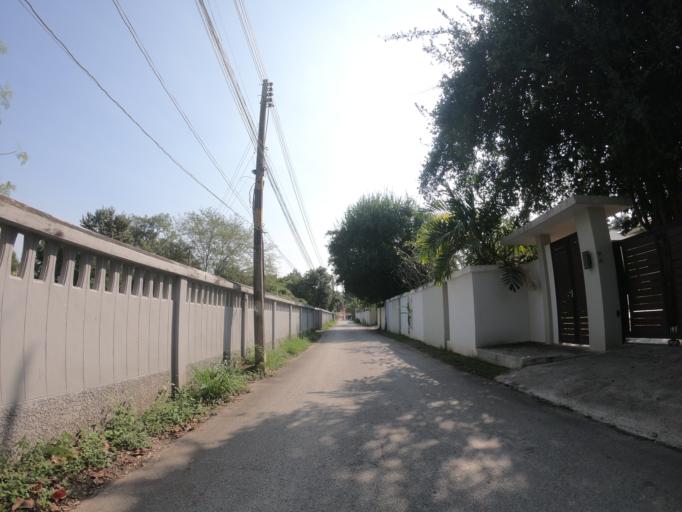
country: TH
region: Chiang Mai
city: Chiang Mai
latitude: 18.7753
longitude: 99.0108
